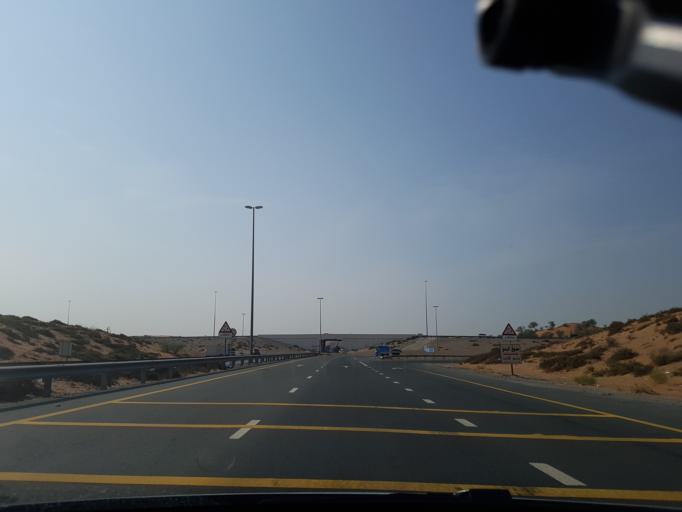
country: AE
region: Umm al Qaywayn
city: Umm al Qaywayn
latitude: 25.5275
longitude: 55.7263
